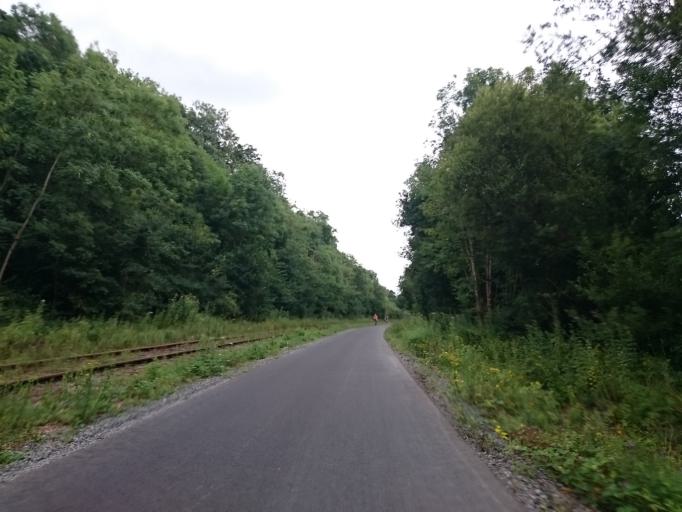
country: FR
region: Lower Normandy
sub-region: Departement du Calvados
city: Clinchamps-sur-Orne
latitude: 49.0821
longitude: -0.4252
